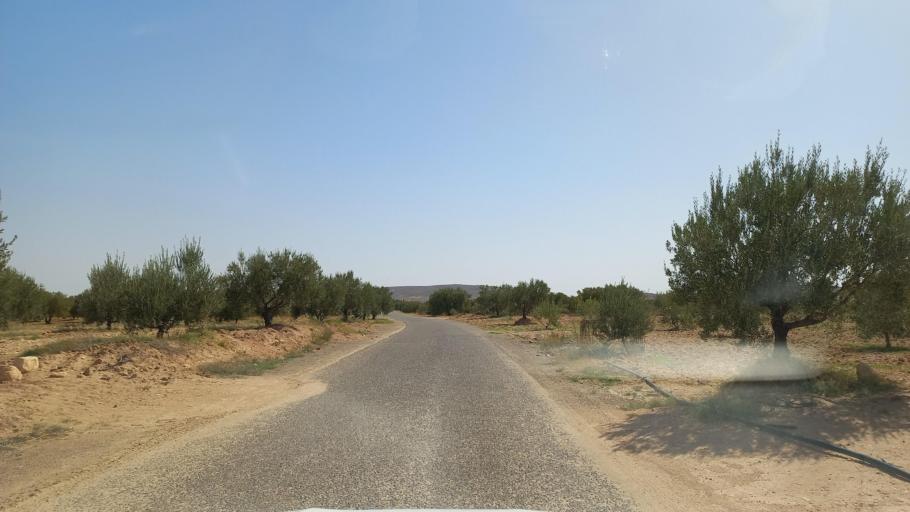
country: TN
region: Al Qasrayn
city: Kasserine
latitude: 35.2175
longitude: 9.0415
